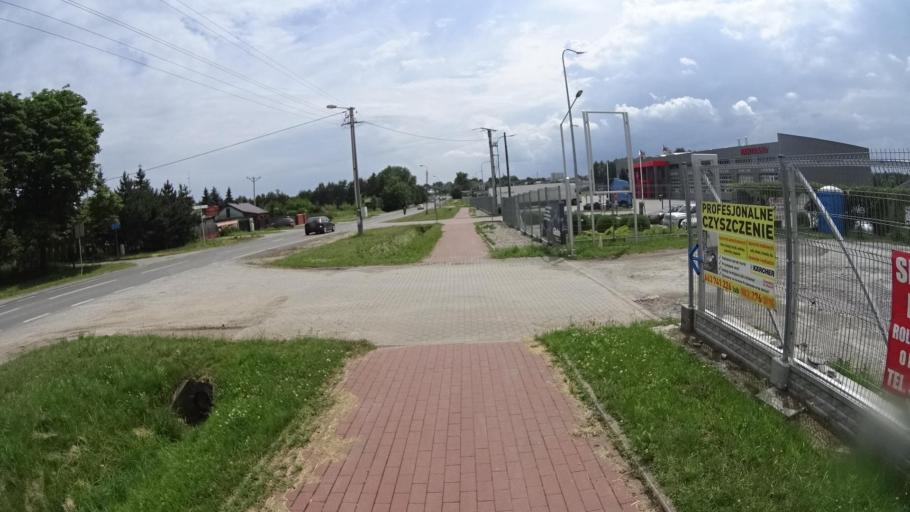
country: PL
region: Masovian Voivodeship
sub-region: Powiat grojecki
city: Grojec
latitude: 51.8775
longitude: 20.8640
